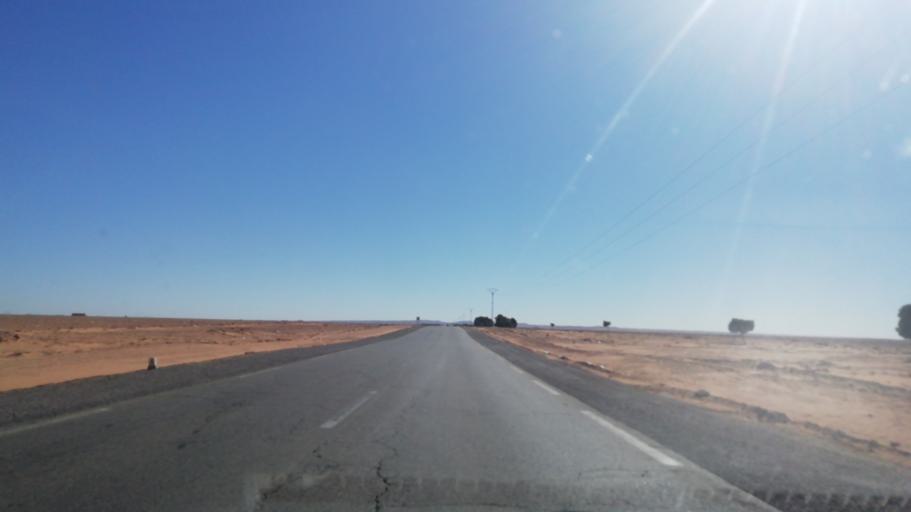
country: DZ
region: Saida
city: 'Ain el Hadjar
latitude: 34.0114
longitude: 0.1168
